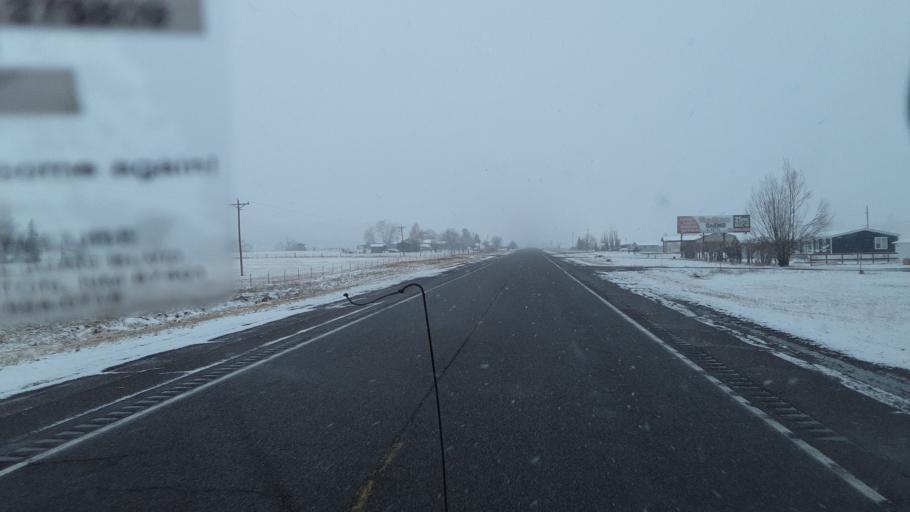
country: US
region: New Mexico
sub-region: Rio Arriba County
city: Chama
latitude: 36.8846
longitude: -106.6083
